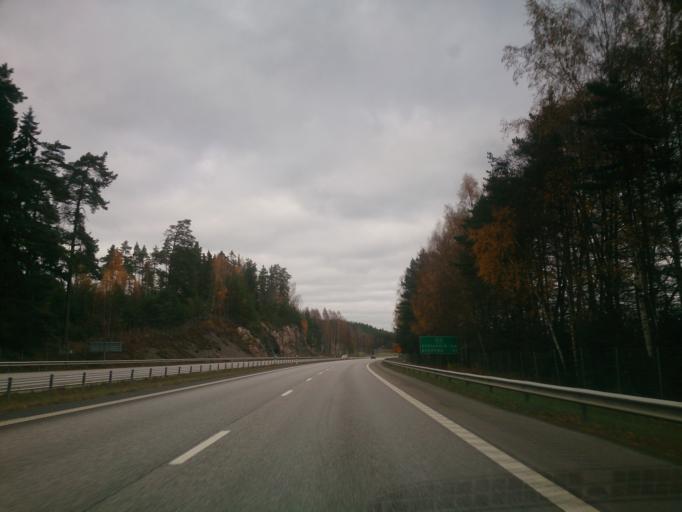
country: SE
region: OEstergoetland
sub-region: Norrkopings Kommun
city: Krokek
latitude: 58.6971
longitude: 16.3375
